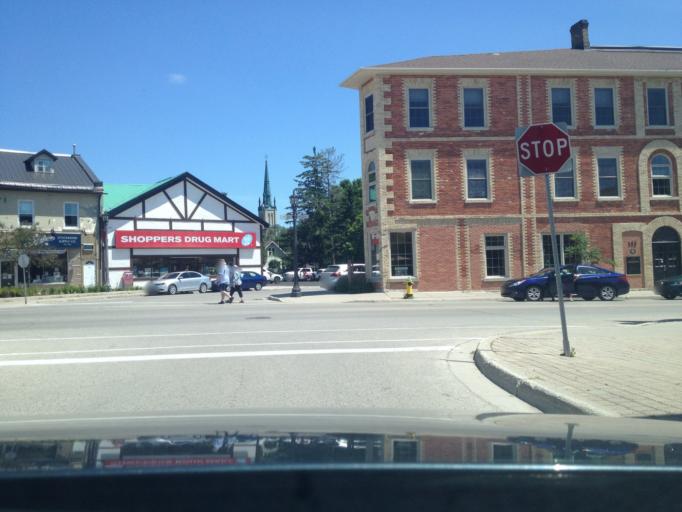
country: CA
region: Ontario
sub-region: Wellington County
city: Guelph
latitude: 43.6830
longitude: -80.4308
